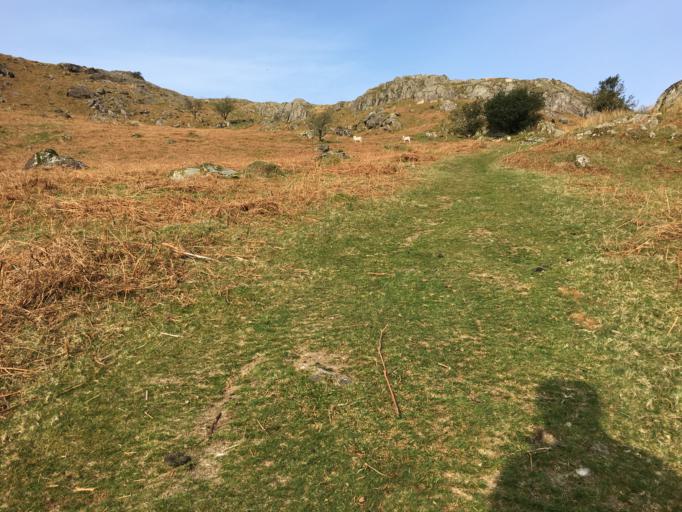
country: GB
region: Wales
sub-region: Gwynedd
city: Porthmadog
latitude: 53.0107
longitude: -4.1237
